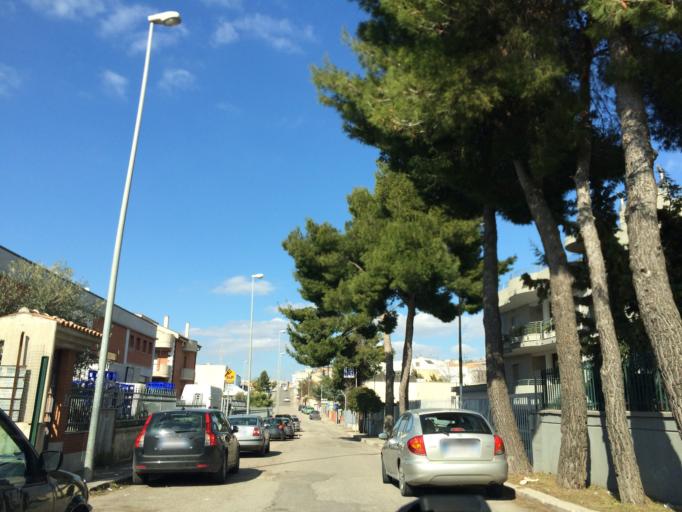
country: IT
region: Basilicate
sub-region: Provincia di Matera
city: Matera
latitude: 40.6702
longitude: 16.5770
